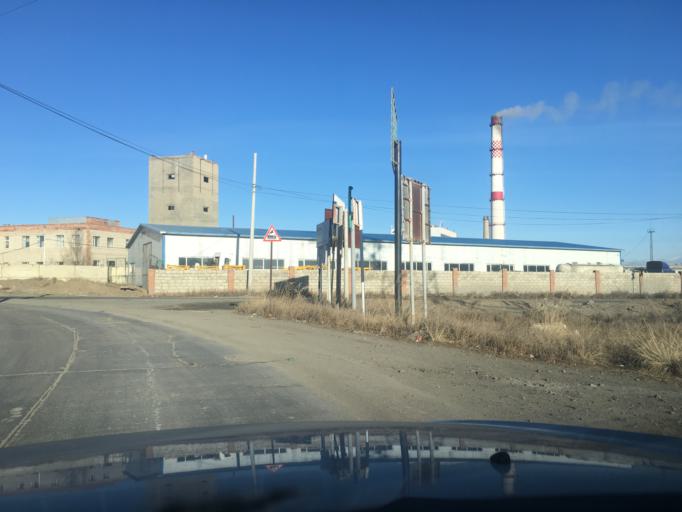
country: MN
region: Ulaanbaatar
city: Ulaanbaatar
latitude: 47.9042
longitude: 106.8024
